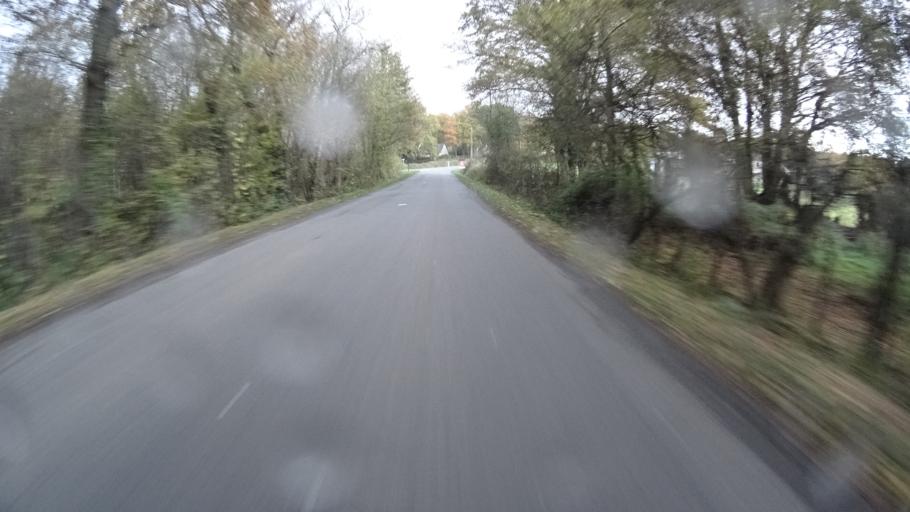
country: FR
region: Pays de la Loire
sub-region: Departement de la Loire-Atlantique
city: Saint-Nicolas-de-Redon
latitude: 47.6729
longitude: -2.0536
